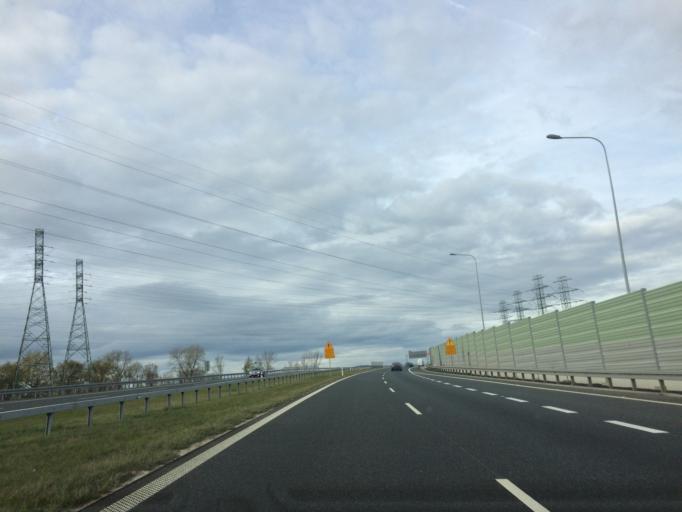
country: PL
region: Lower Silesian Voivodeship
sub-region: Powiat legnicki
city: Milkowice
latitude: 51.1793
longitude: 16.0887
